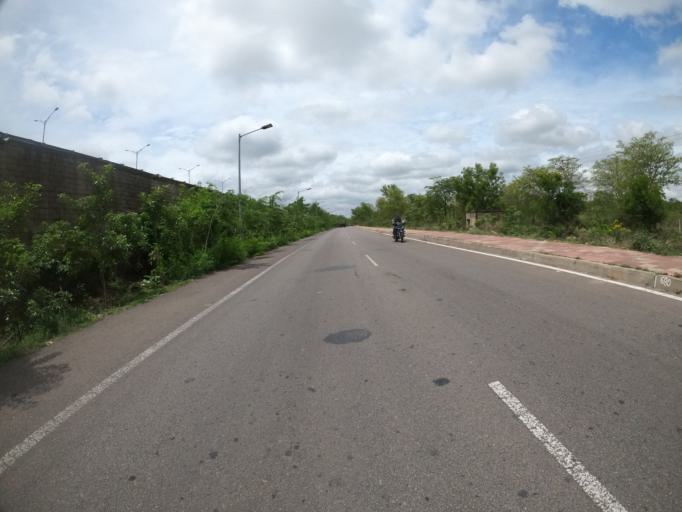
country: IN
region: Telangana
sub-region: Rangareddi
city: Balapur
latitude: 17.2799
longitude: 78.3824
